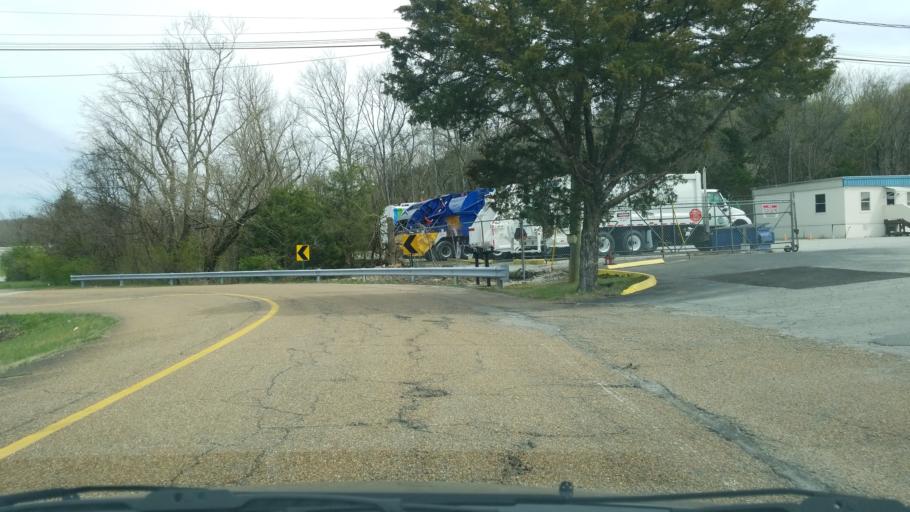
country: US
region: Tennessee
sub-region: Hamilton County
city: Harrison
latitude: 35.0635
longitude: -85.1295
